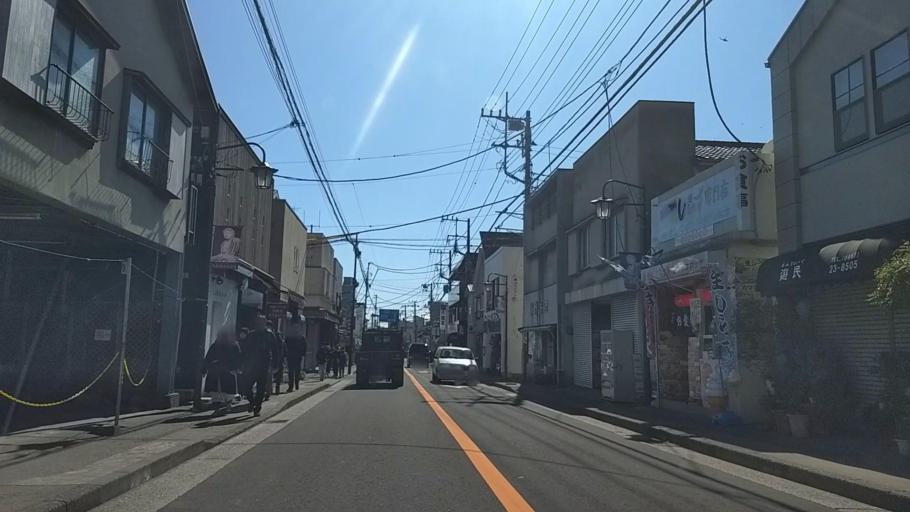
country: JP
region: Kanagawa
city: Kamakura
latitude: 35.3142
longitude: 139.5350
